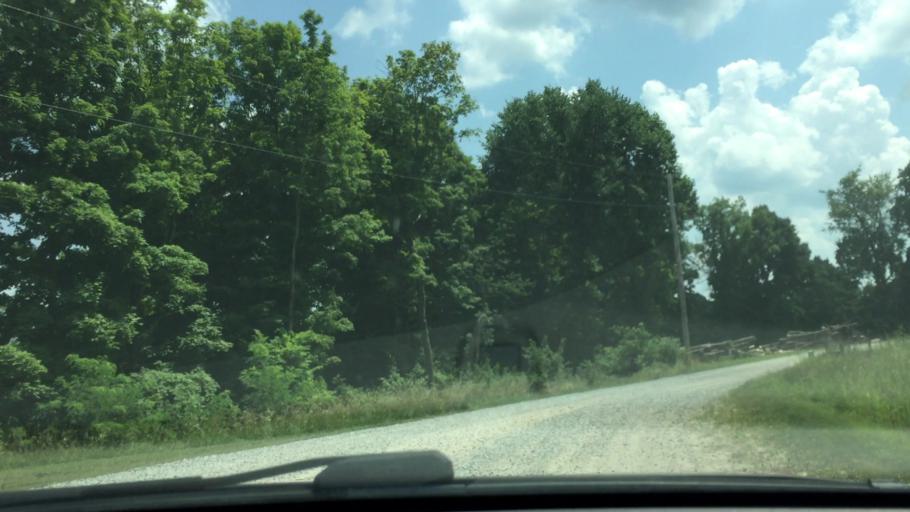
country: US
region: West Virginia
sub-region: Wetzel County
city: New Martinsville
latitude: 39.7333
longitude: -80.7441
